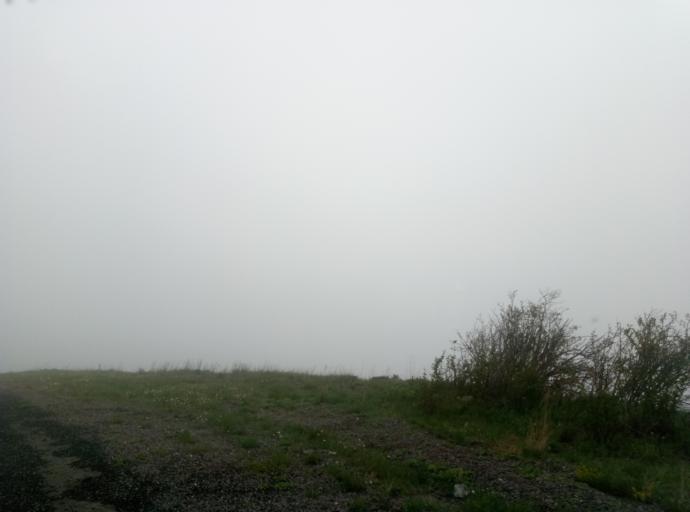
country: TR
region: Sivas
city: Serefiye
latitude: 40.1629
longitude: 37.8602
